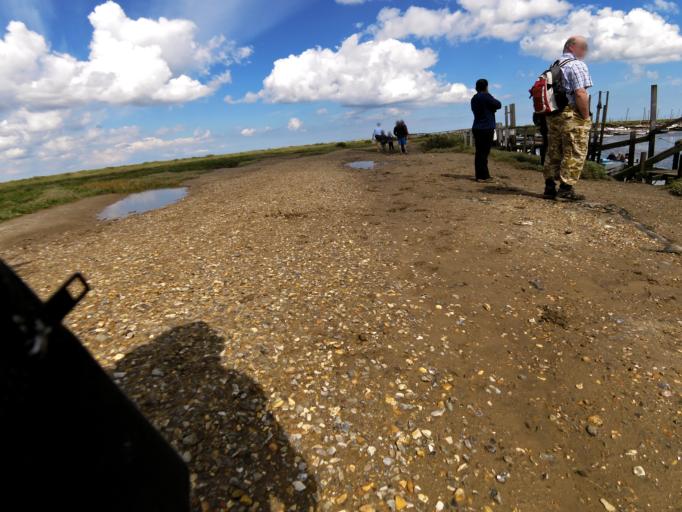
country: GB
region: England
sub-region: Norfolk
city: Briston
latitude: 52.9607
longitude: 0.9825
